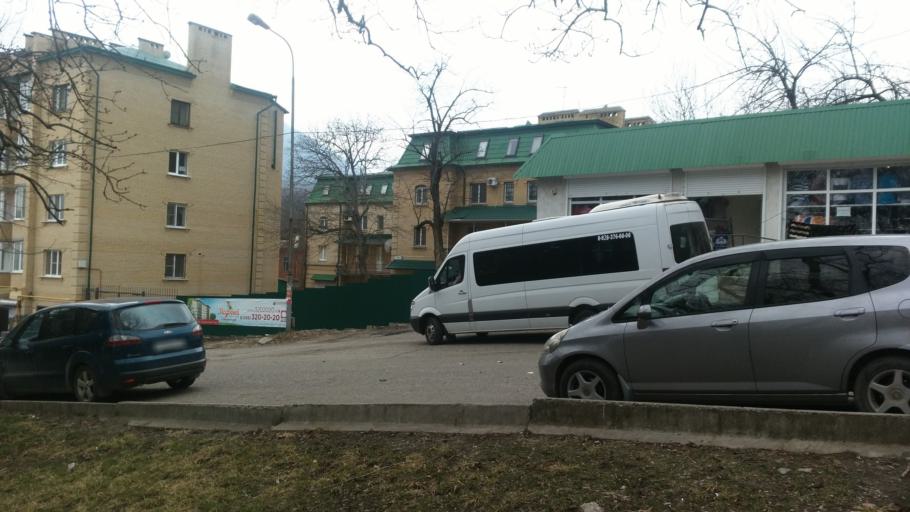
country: RU
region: Stavropol'skiy
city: Zheleznovodsk
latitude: 44.1338
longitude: 43.0365
